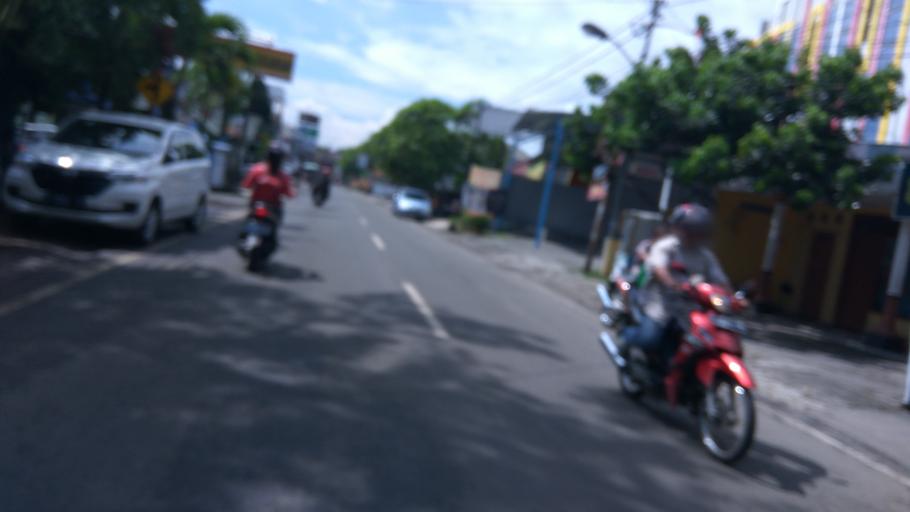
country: ID
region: Central Java
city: Ungaran
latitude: -7.1268
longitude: 110.4090
